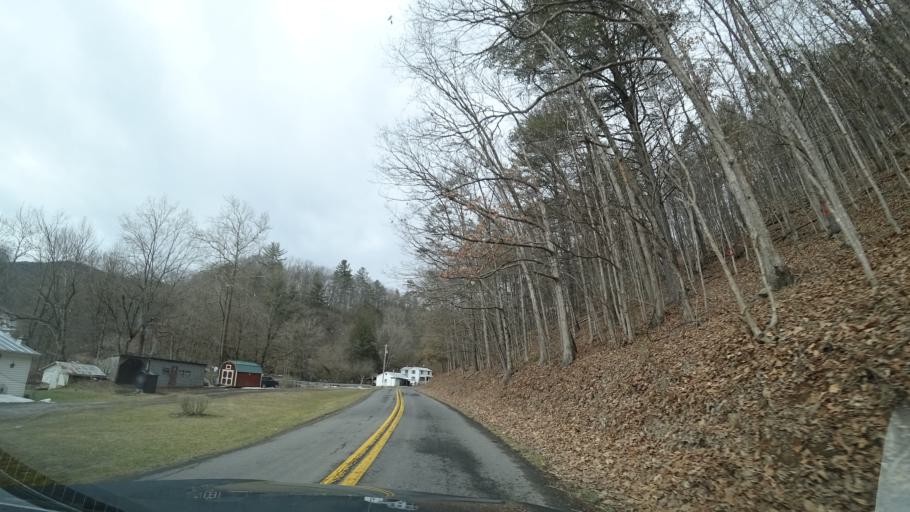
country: US
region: Virginia
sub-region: Shenandoah County
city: Basye
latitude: 38.8815
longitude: -78.8923
